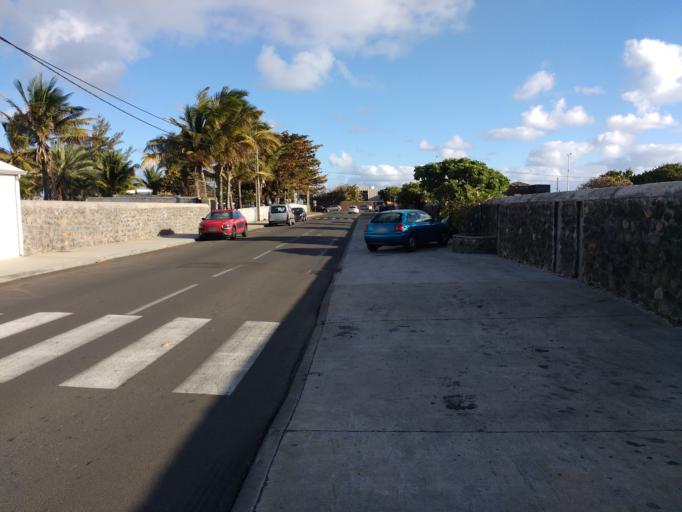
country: RE
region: Reunion
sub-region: Reunion
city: Saint-Pierre
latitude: -21.3425
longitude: 55.4684
